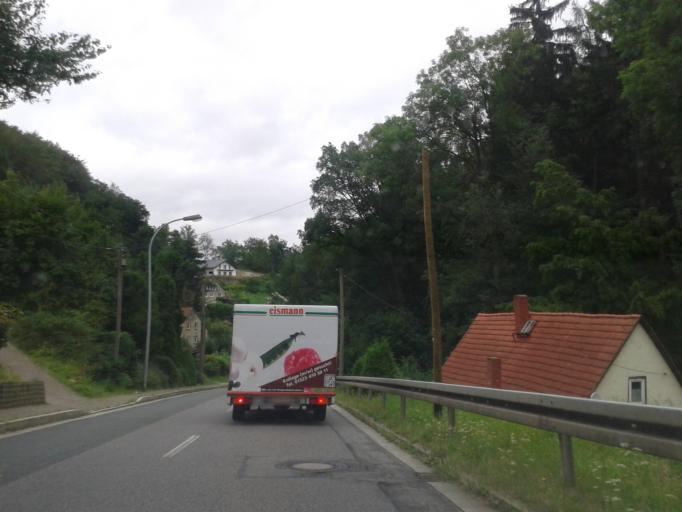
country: DE
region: Saxony
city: Tharandt
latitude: 50.9837
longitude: 13.5747
